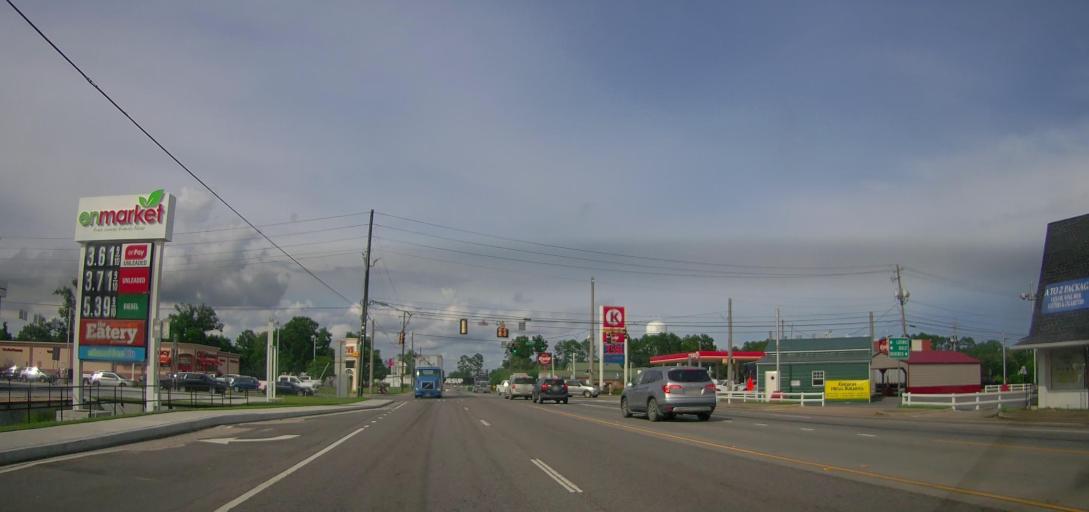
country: US
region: Georgia
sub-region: Wayne County
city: Jesup
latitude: 31.6089
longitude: -81.8836
